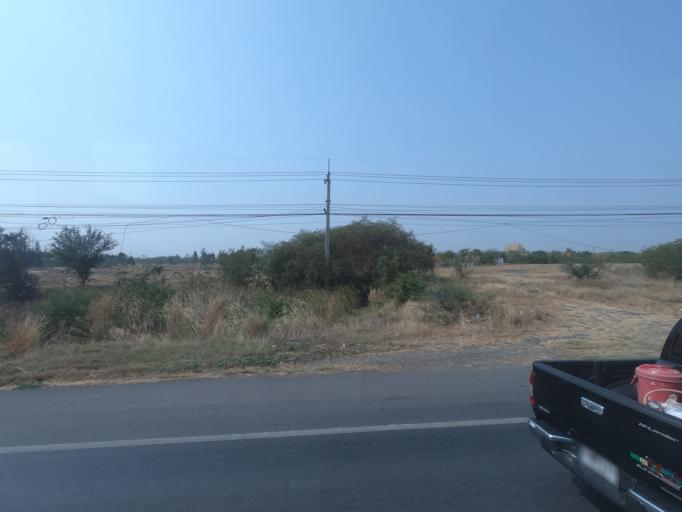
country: TH
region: Nakhon Ratchasima
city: Phimai
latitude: 15.3099
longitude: 102.4264
